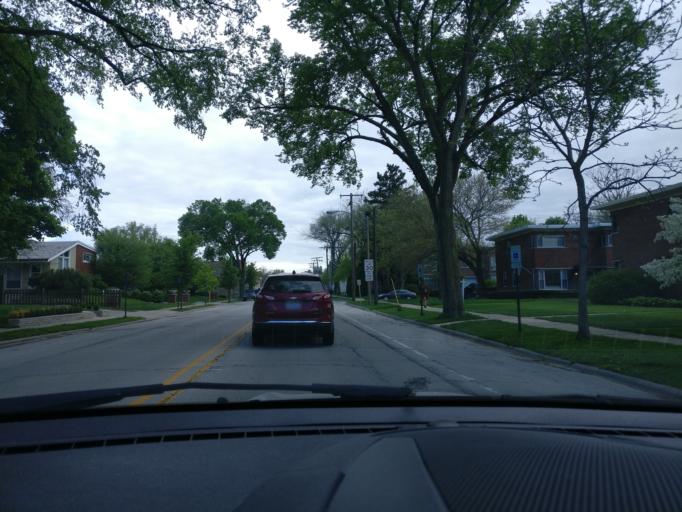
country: US
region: Illinois
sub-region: Cook County
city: Wilmette
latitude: 42.0742
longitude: -87.7226
